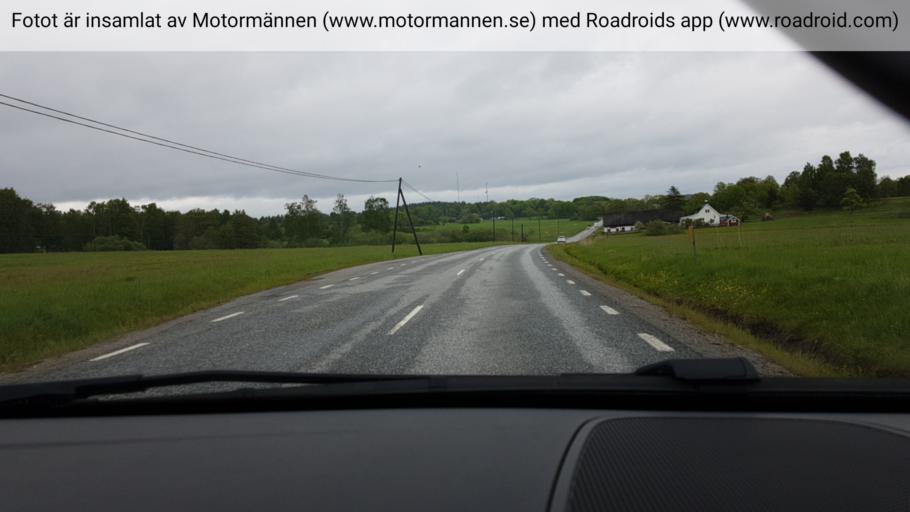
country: SE
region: Stockholm
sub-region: Haninge Kommun
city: Jordbro
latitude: 58.9997
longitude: 18.1088
